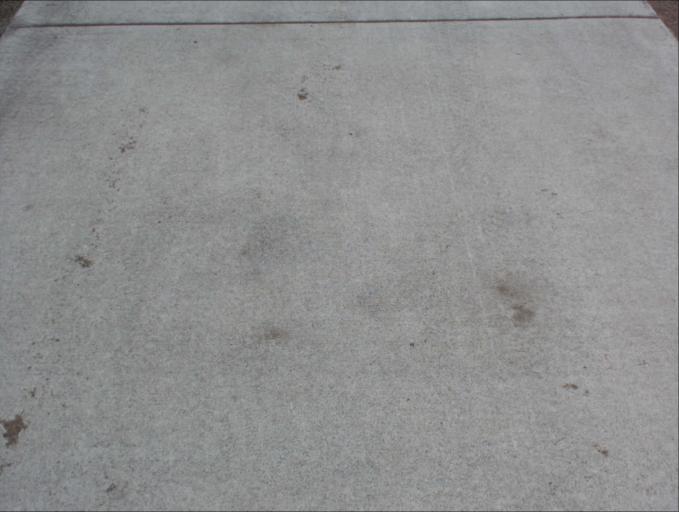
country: AU
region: Queensland
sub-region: Logan
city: Windaroo
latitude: -27.7272
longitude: 153.1930
